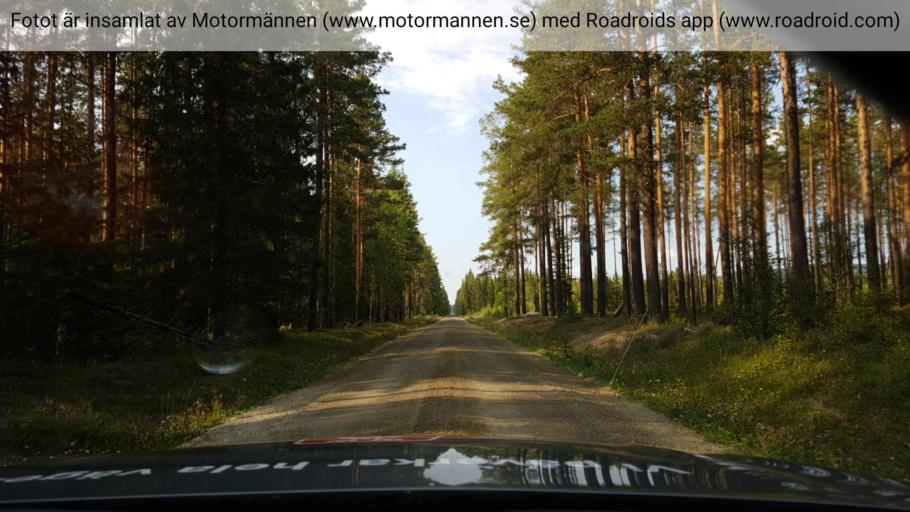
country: SE
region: Jaemtland
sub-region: Braecke Kommun
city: Braecke
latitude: 62.4895
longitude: 14.9240
